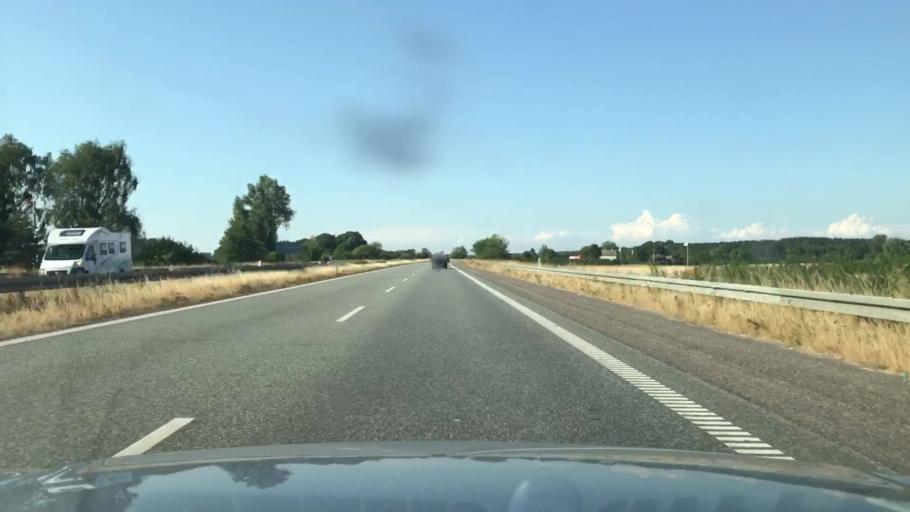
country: DK
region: Zealand
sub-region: Koge Kommune
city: Bjaeverskov
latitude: 55.3941
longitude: 12.0953
